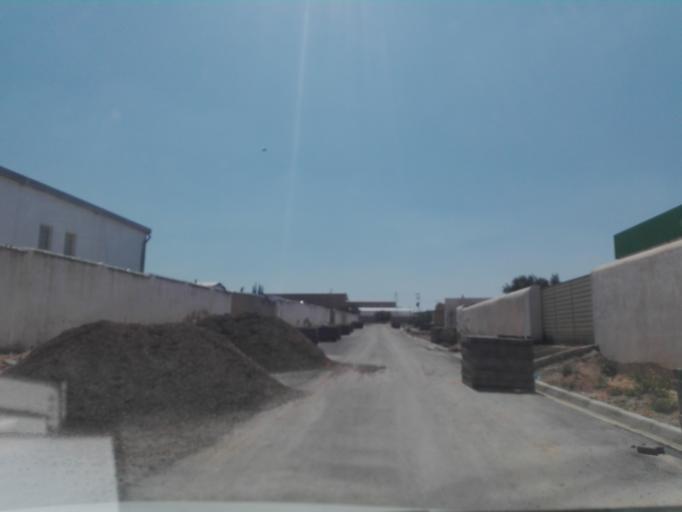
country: TN
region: Safaqis
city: Sfax
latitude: 34.7250
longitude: 10.5136
